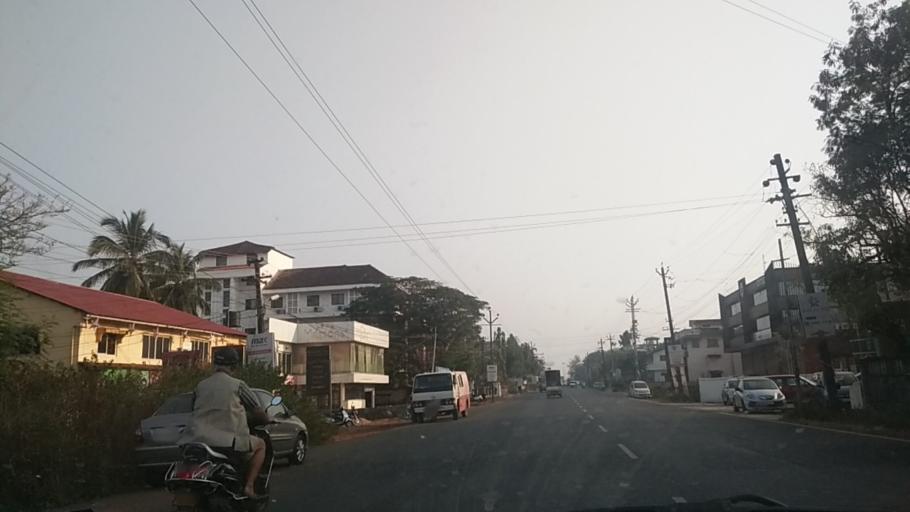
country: IN
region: Goa
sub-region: North Goa
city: Serula
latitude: 15.5365
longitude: 73.8232
